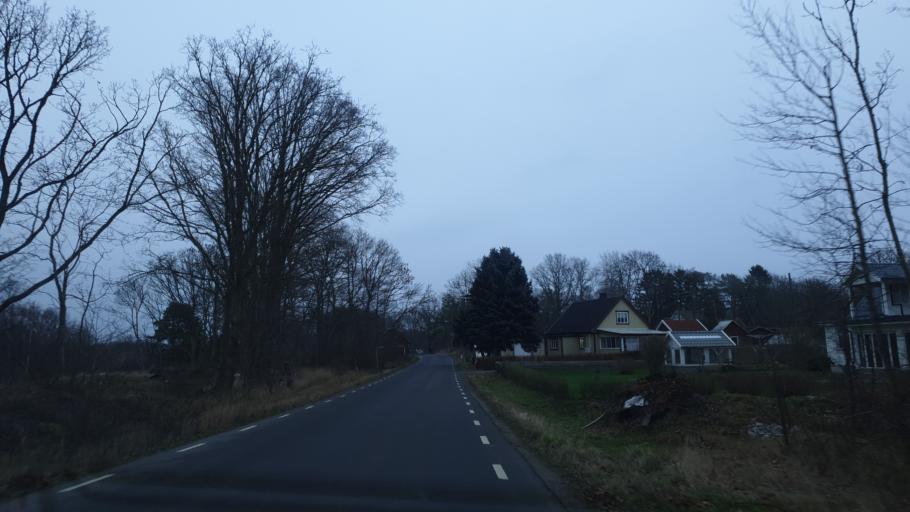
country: SE
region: Blekinge
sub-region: Karlskrona Kommun
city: Sturko
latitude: 56.1123
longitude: 15.6517
